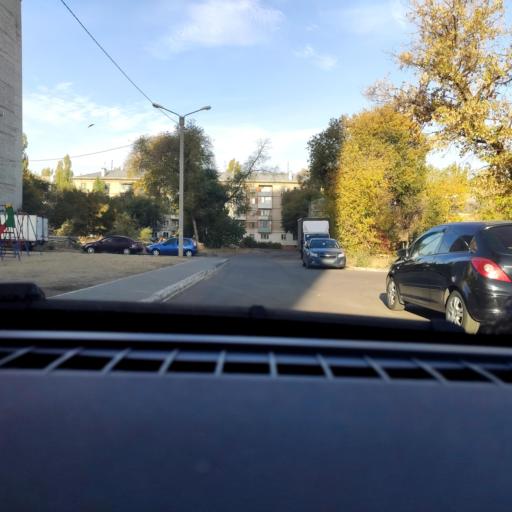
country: RU
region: Voronezj
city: Maslovka
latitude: 51.6180
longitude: 39.2480
